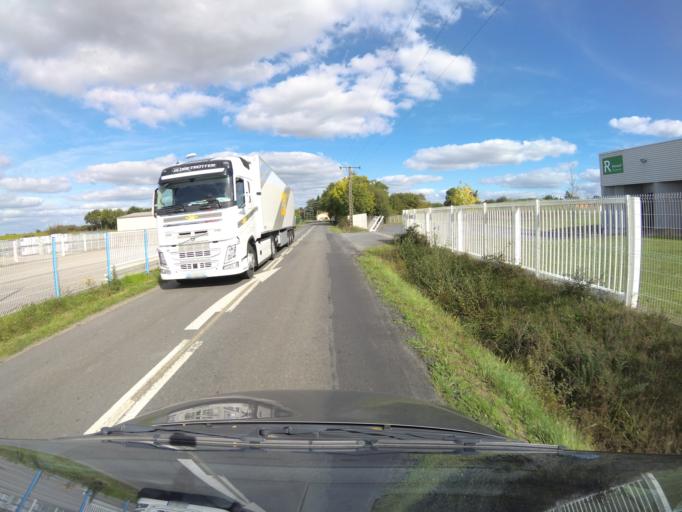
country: FR
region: Pays de la Loire
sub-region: Departement de la Loire-Atlantique
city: Le Pallet
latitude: 47.1522
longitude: -1.3459
